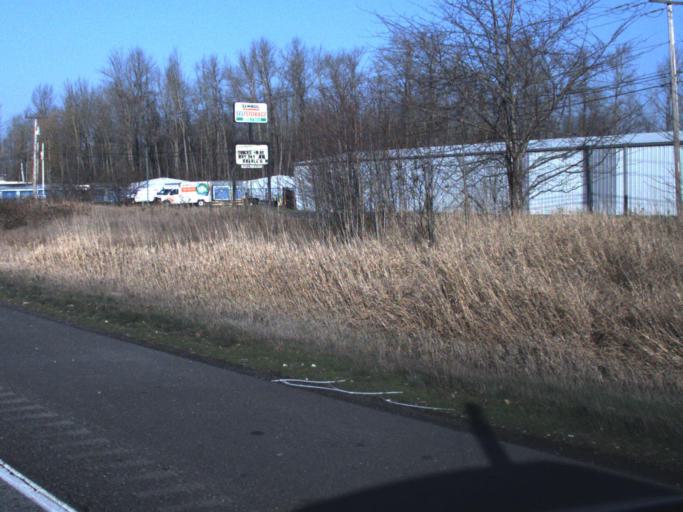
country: US
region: Washington
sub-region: Whatcom County
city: Ferndale
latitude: 48.8394
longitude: -122.5695
